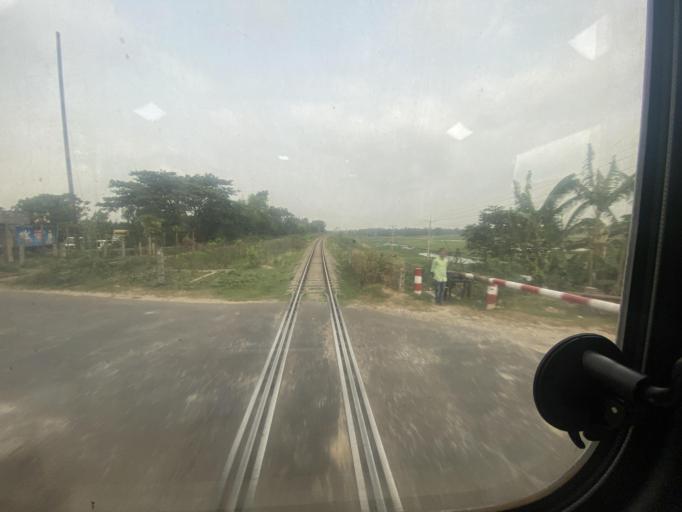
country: BD
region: Dhaka
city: Tungi
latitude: 23.9338
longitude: 90.4944
